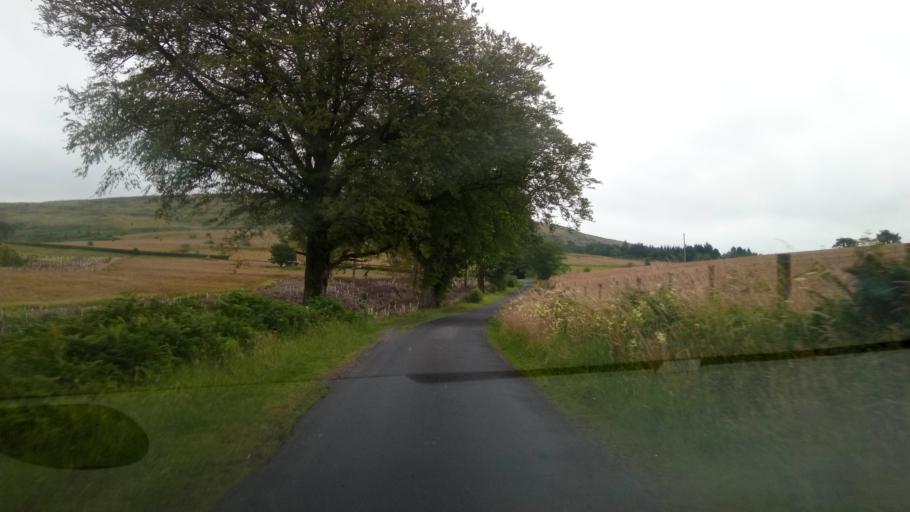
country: GB
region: Scotland
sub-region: Dumfries and Galloway
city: Langholm
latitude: 55.1577
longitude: -2.9937
